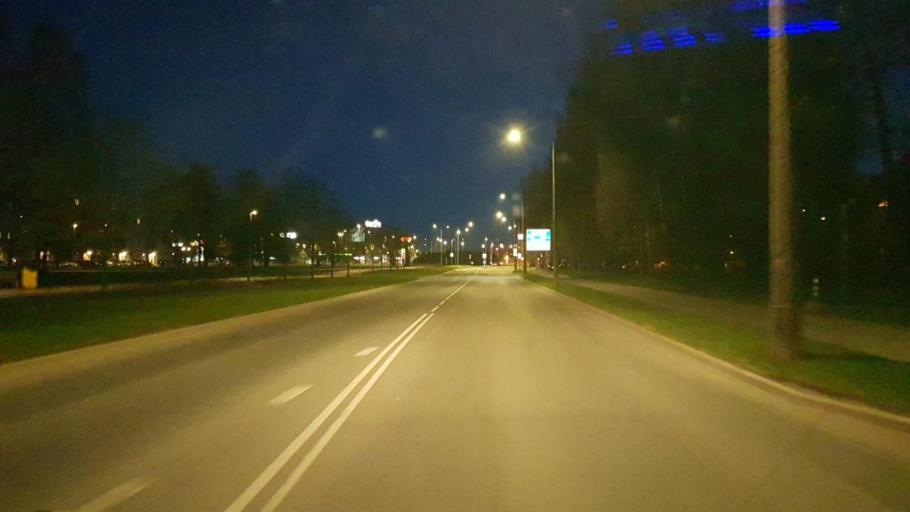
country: EE
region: Tartu
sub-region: Tartu linn
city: Tartu
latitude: 58.3770
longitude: 26.7512
